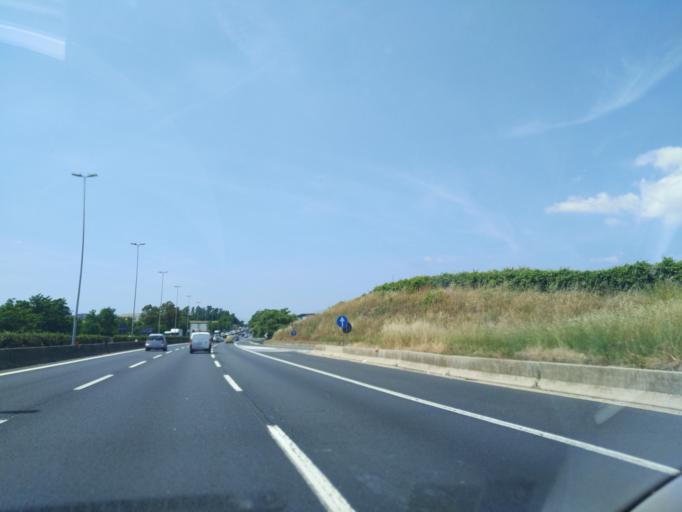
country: IT
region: Latium
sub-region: Citta metropolitana di Roma Capitale
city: Selcetta
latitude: 41.7944
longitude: 12.5097
